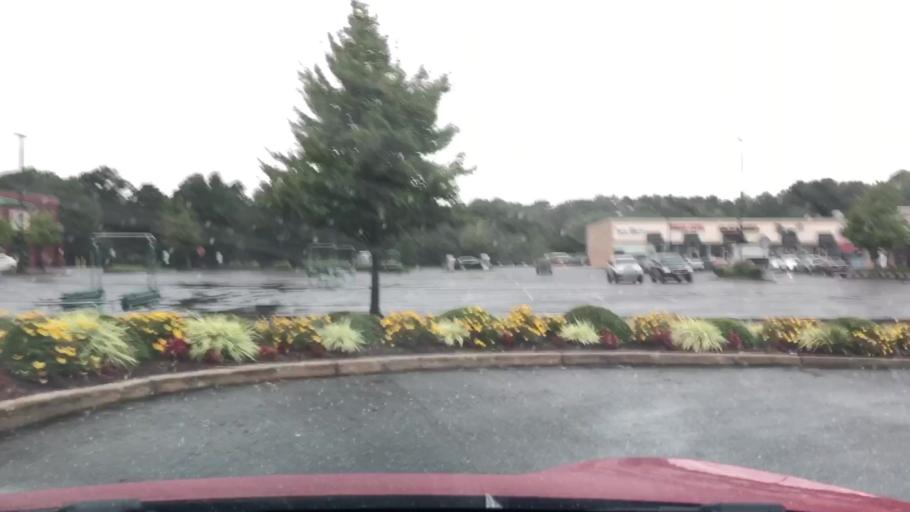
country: US
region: New Jersey
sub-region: Atlantic County
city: Northfield
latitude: 39.3928
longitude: -74.5616
